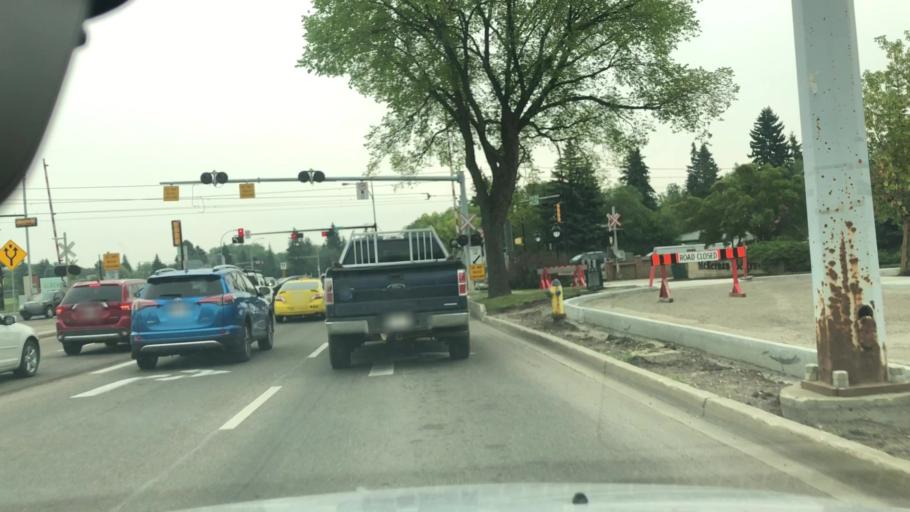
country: CA
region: Alberta
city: Edmonton
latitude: 53.5166
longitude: -113.5269
